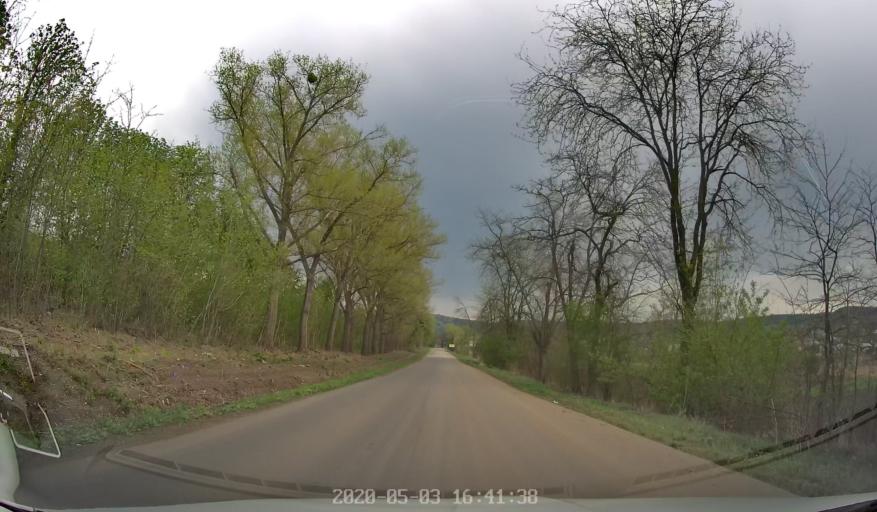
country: MD
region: Stinga Nistrului
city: Bucovat
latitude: 47.1652
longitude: 28.4106
